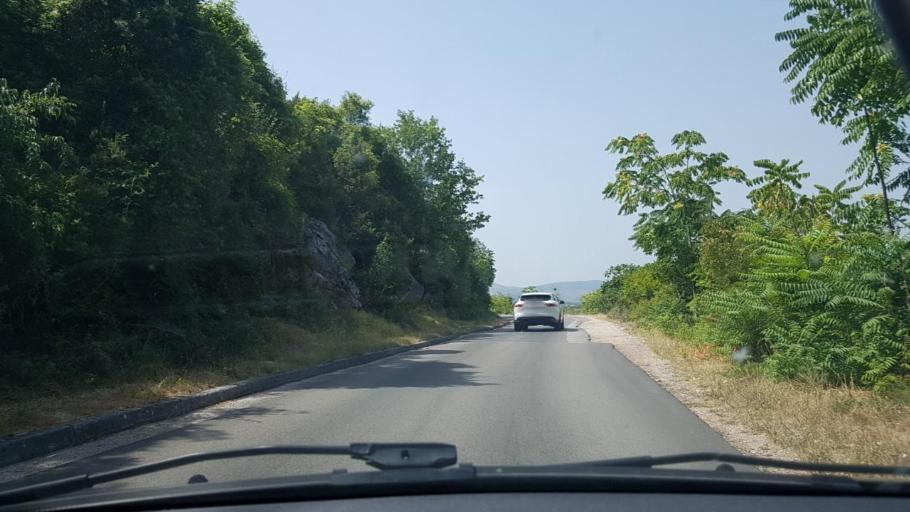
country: BA
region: Federation of Bosnia and Herzegovina
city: Tasovcici
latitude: 43.0286
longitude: 17.7456
